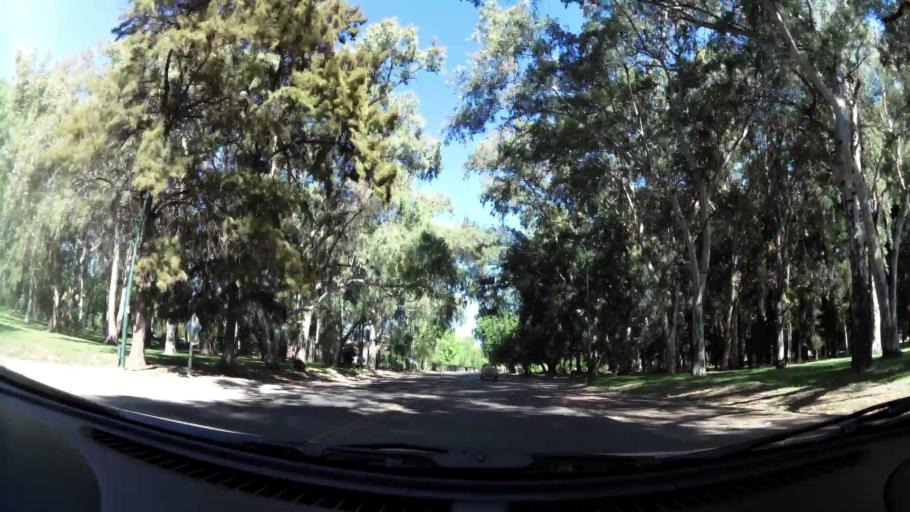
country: AR
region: Mendoza
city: Mendoza
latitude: -32.8928
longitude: -68.8735
